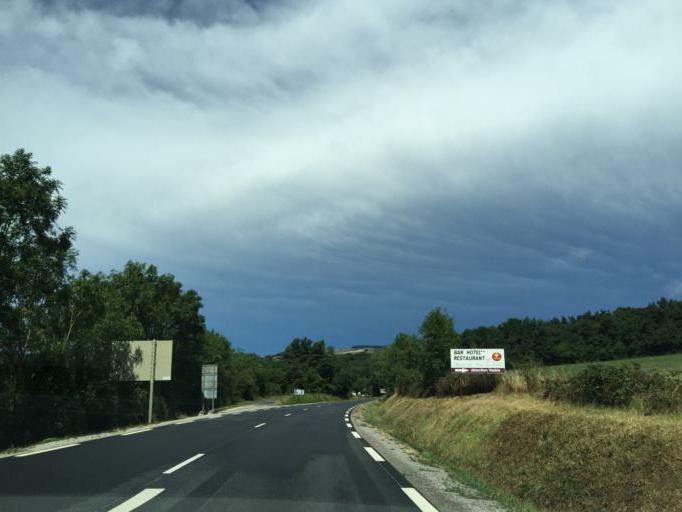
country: FR
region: Midi-Pyrenees
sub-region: Departement de l'Aveyron
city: Severac-le-Chateau
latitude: 44.2295
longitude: 2.9871
